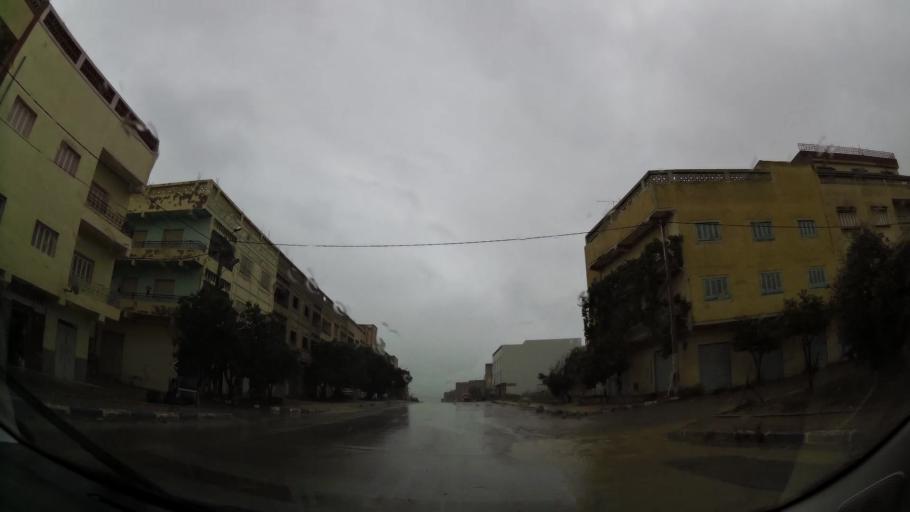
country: MA
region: Oriental
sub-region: Nador
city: Midar
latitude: 34.8867
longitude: -3.7273
